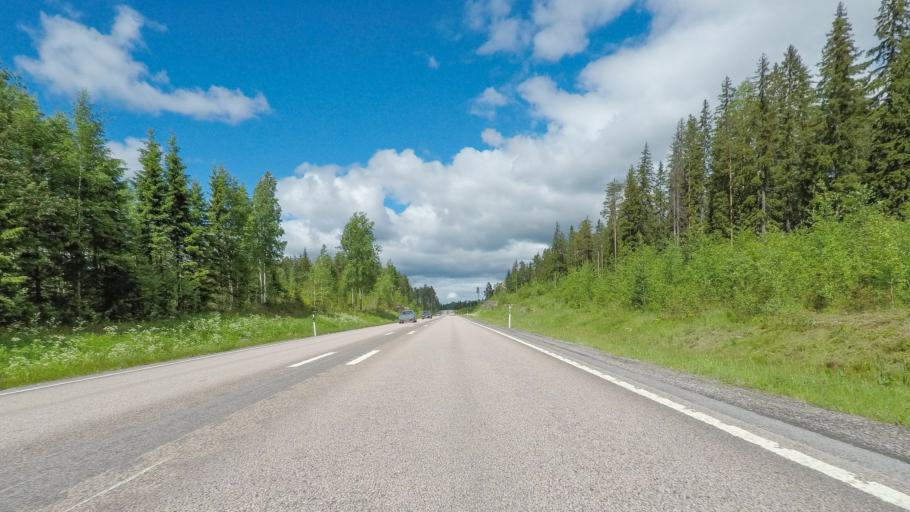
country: FI
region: Paijanne Tavastia
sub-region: Lahti
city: Heinola
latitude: 61.3799
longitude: 26.0511
